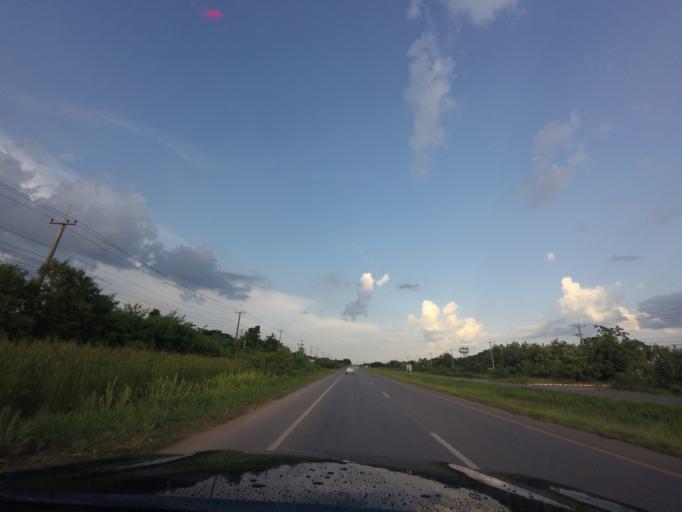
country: TH
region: Khon Kaen
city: Khon Kaen
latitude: 16.3964
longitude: 102.8585
